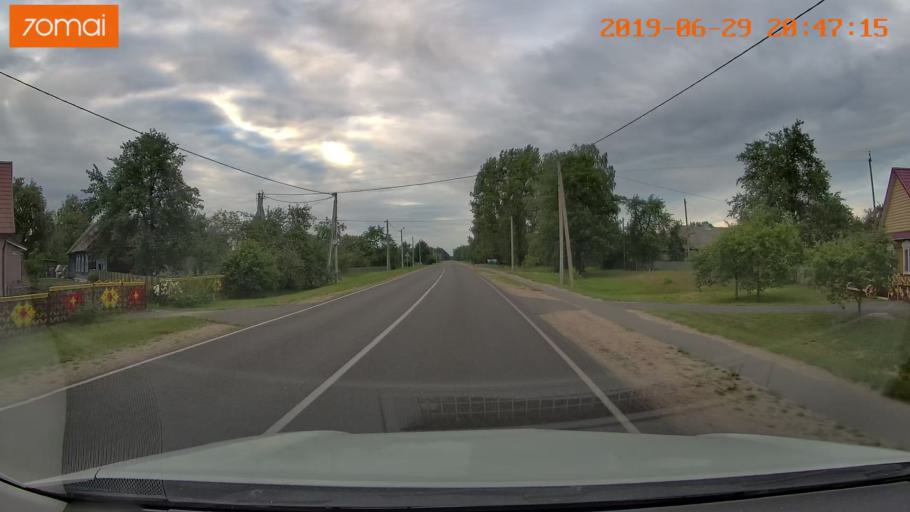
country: BY
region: Brest
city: Hantsavichy
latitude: 52.6367
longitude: 26.3150
